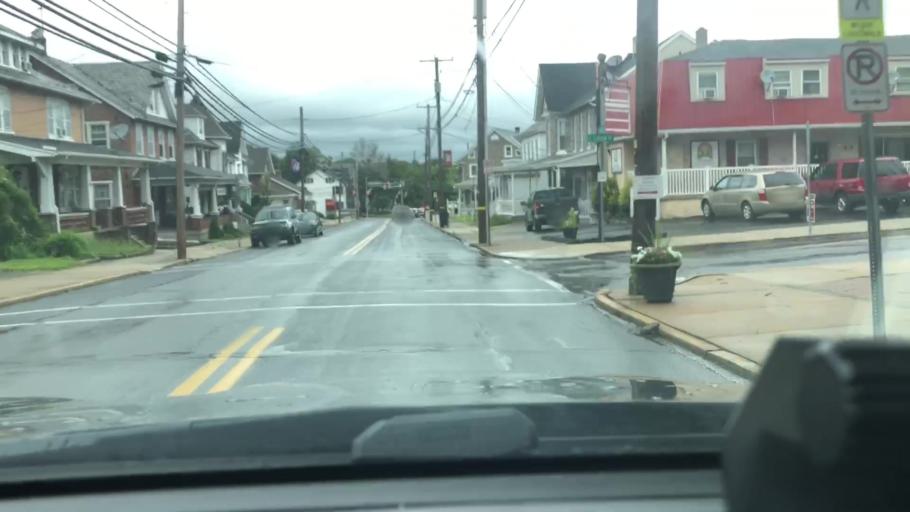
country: US
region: Pennsylvania
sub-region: Lehigh County
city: Coopersburg
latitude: 40.5100
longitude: -75.3916
